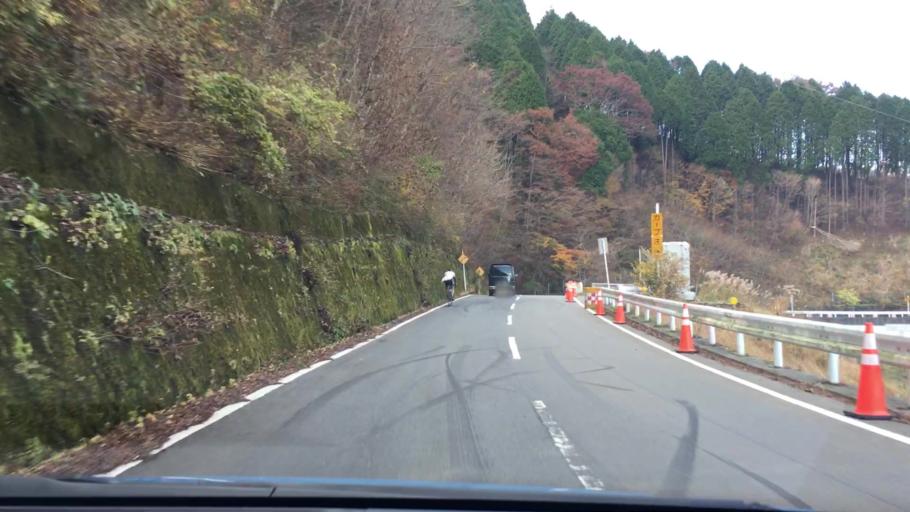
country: JP
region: Shizuoka
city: Gotemba
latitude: 35.4012
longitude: 138.9269
